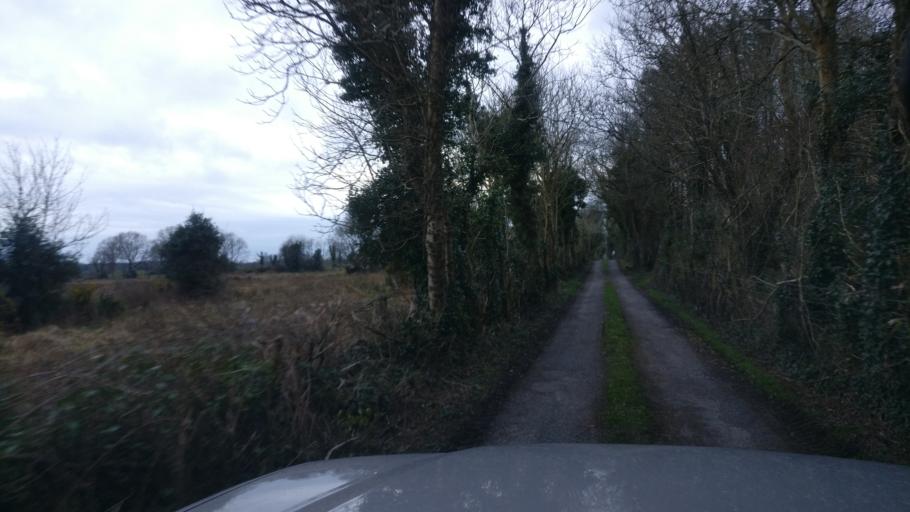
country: IE
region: Connaught
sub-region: County Galway
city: Loughrea
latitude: 53.2526
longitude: -8.4494
